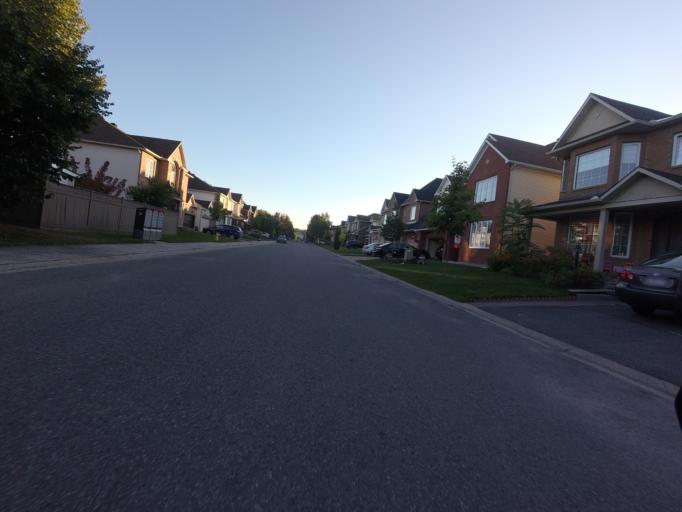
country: CA
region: Ontario
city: Bells Corners
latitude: 45.2802
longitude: -75.7075
